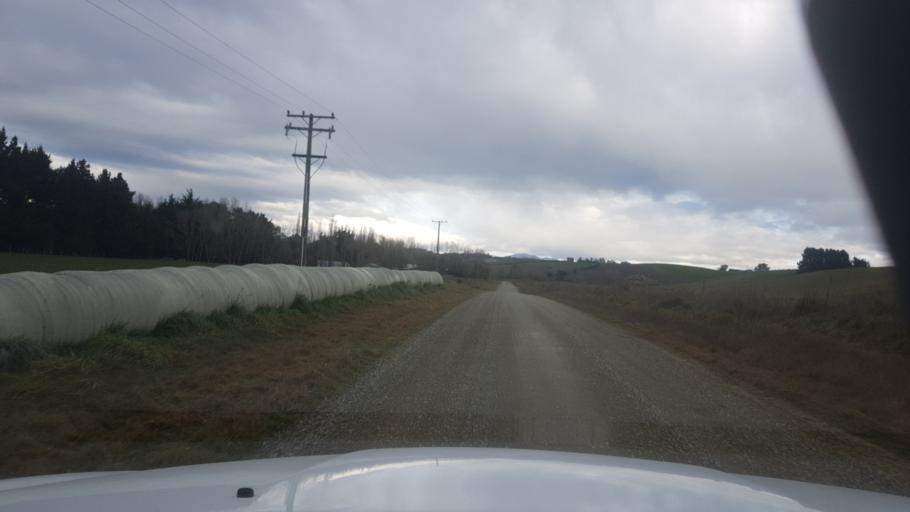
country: NZ
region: Canterbury
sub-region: Timaru District
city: Pleasant Point
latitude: -44.3391
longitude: 171.1749
